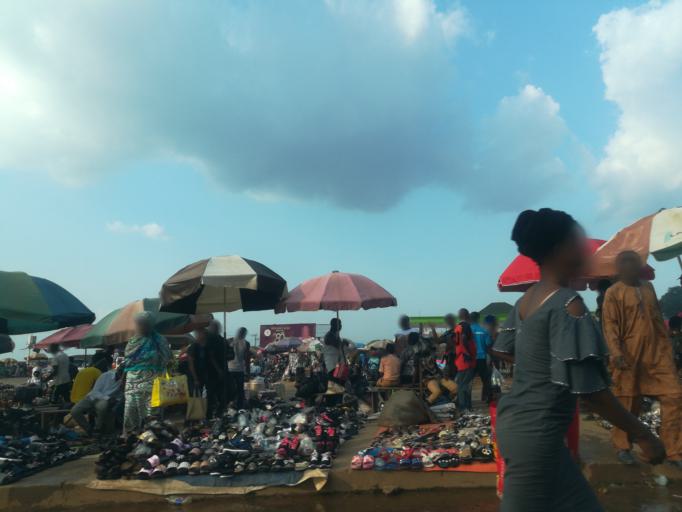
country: NG
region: Oyo
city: Moniya
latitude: 7.4682
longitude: 3.9128
